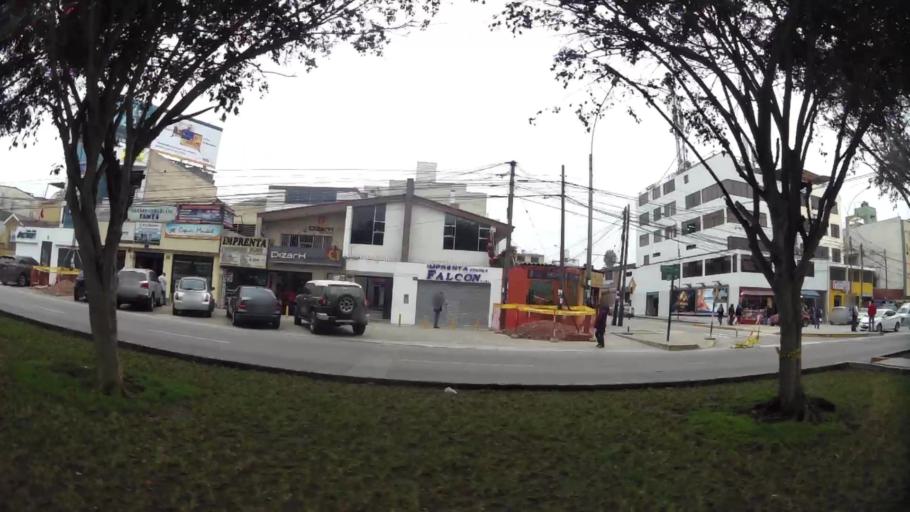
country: PE
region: Lima
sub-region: Lima
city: Surco
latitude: -12.1304
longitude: -76.9805
